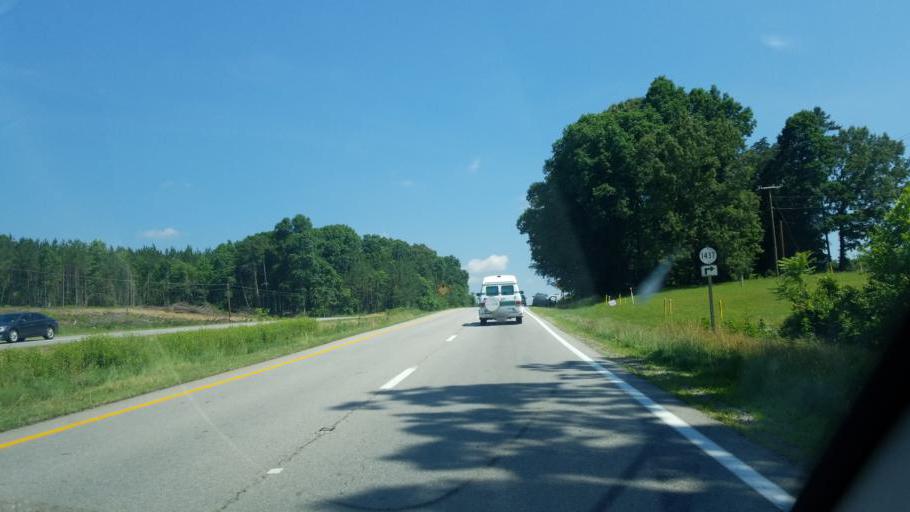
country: US
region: Virginia
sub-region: Pittsylvania County
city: Chatham
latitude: 36.7822
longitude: -79.3939
